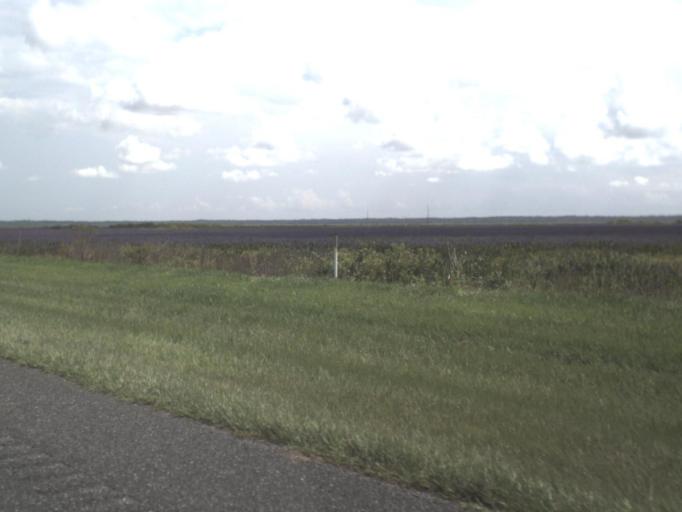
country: US
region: Florida
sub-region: Alachua County
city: Gainesville
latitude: 29.5652
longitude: -82.3329
